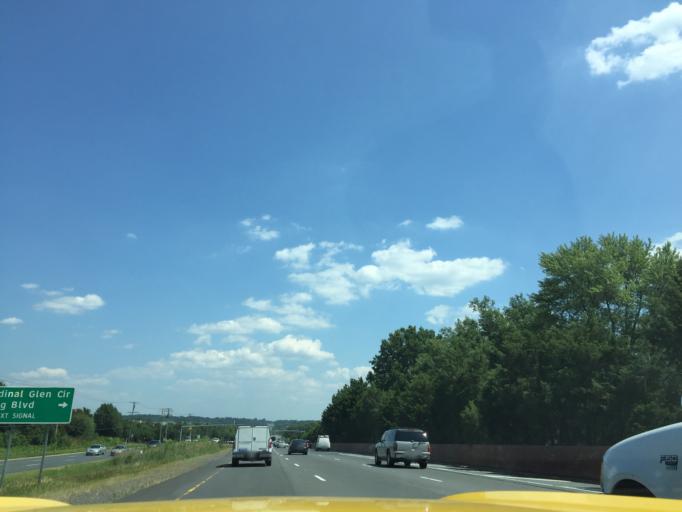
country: US
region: Virginia
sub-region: Loudoun County
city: Sugarland Run
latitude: 39.0229
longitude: -77.3875
